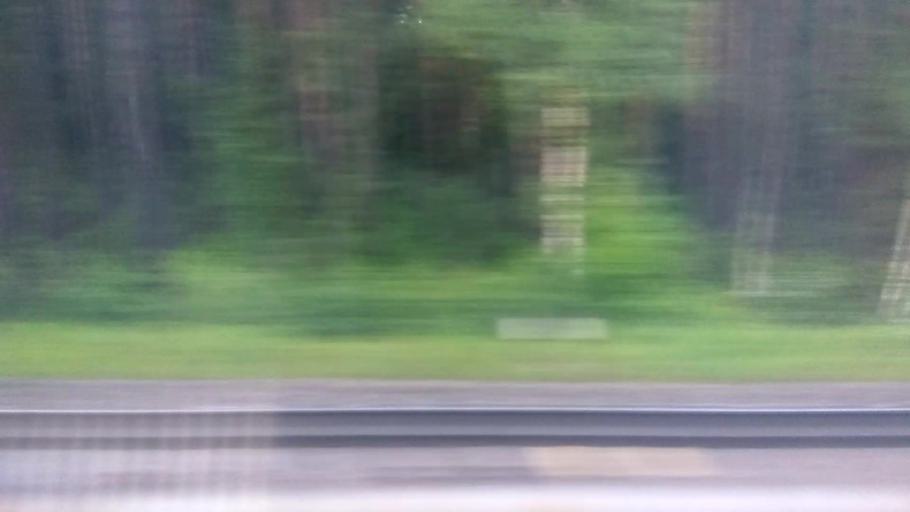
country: RU
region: Moskovskaya
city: Vostryakovo
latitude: 55.3673
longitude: 37.8259
